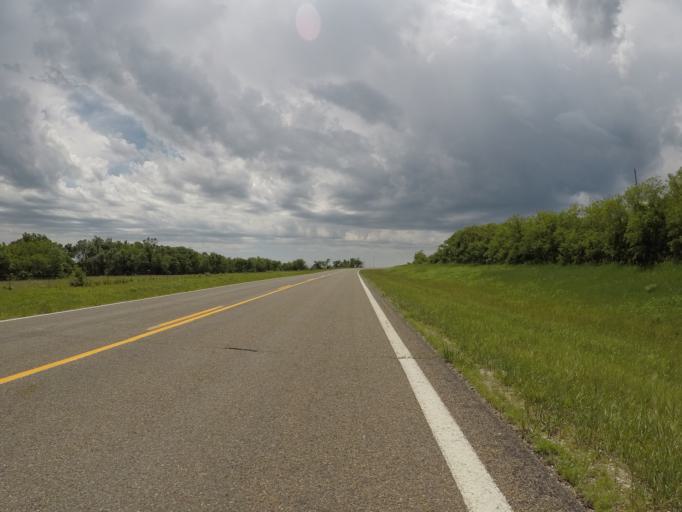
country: US
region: Kansas
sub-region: Wabaunsee County
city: Alma
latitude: 38.8601
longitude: -96.3726
